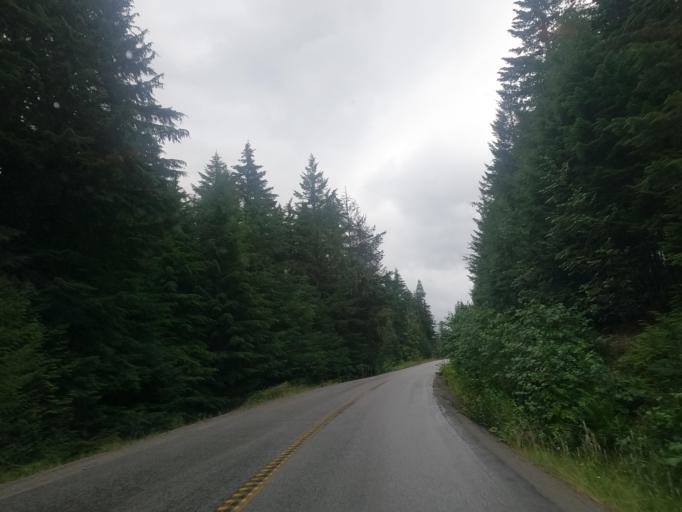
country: CA
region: British Columbia
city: Pemberton
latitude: 50.3191
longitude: -122.5631
